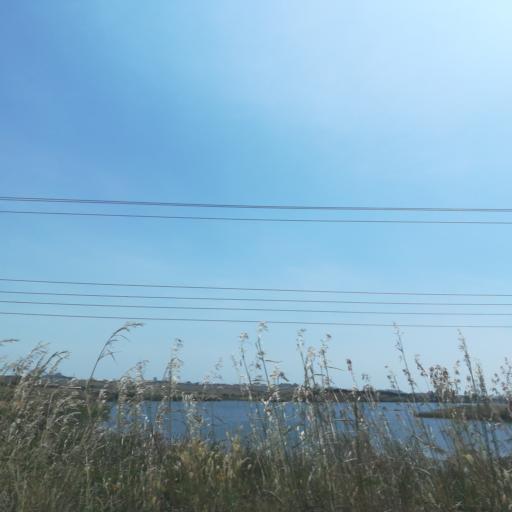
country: NG
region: Plateau
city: Bukuru
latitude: 9.8467
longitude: 8.9156
